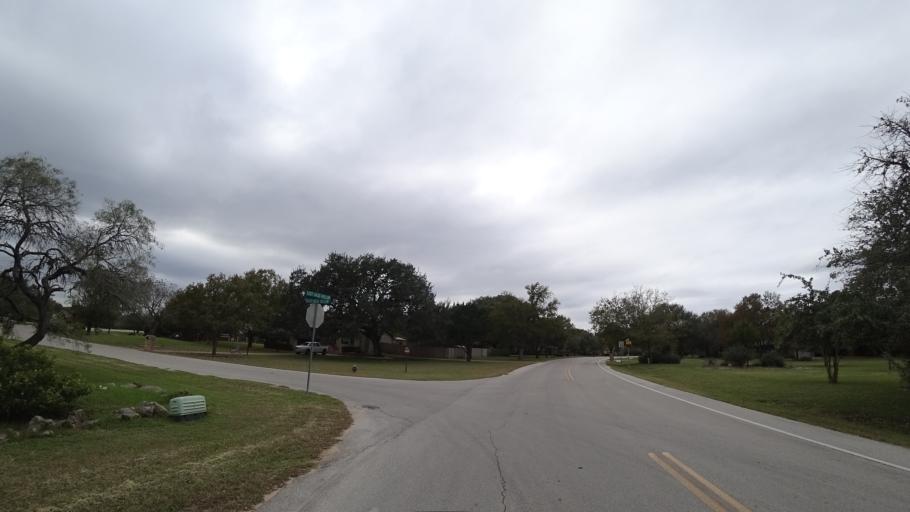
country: US
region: Texas
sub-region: Travis County
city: Shady Hollow
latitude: 30.1556
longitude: -97.8699
